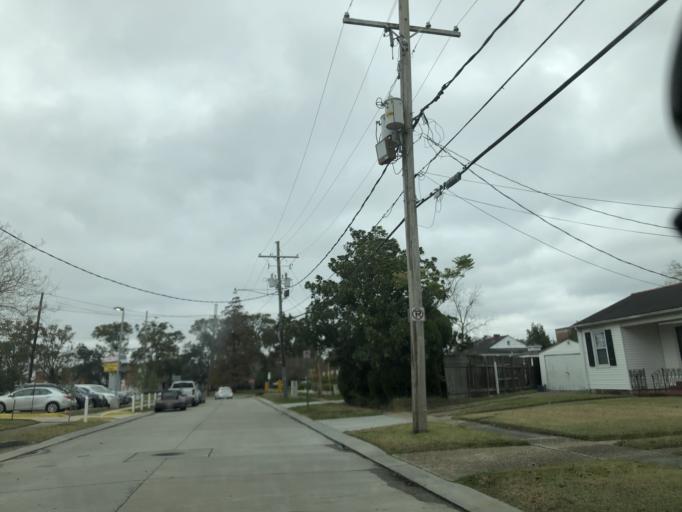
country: US
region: Louisiana
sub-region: Jefferson Parish
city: Metairie
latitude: 29.9772
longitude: -90.1539
